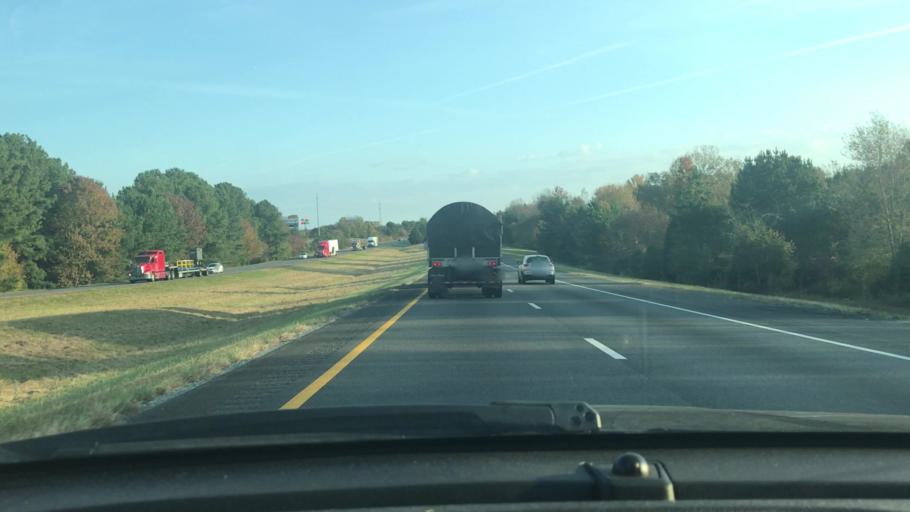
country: US
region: Tennessee
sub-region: Sumner County
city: White House
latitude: 36.4556
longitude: -86.6920
